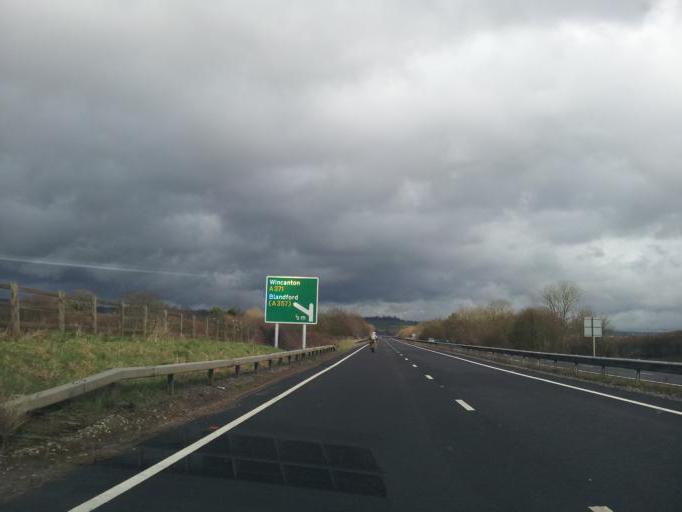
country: GB
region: England
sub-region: Somerset
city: Wincanton
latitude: 51.0461
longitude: -2.4374
